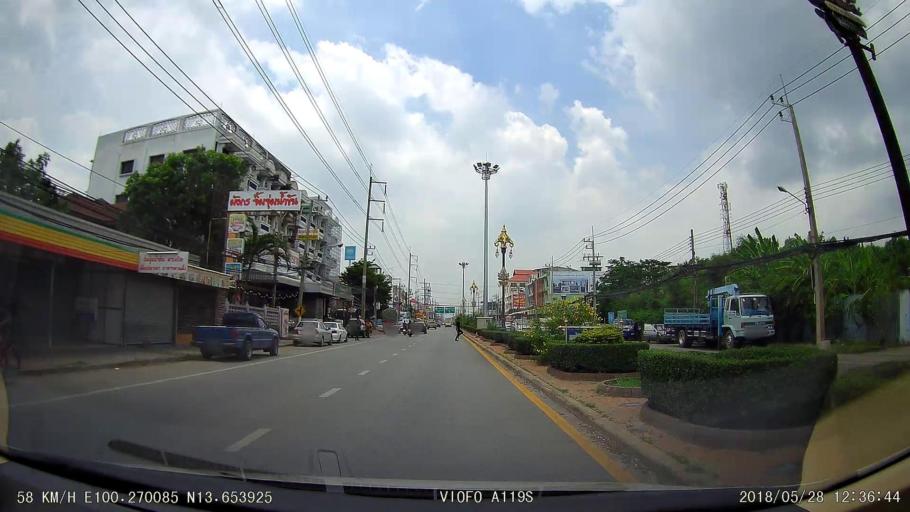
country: TH
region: Samut Sakhon
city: Krathum Baen
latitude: 13.6538
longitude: 100.2704
